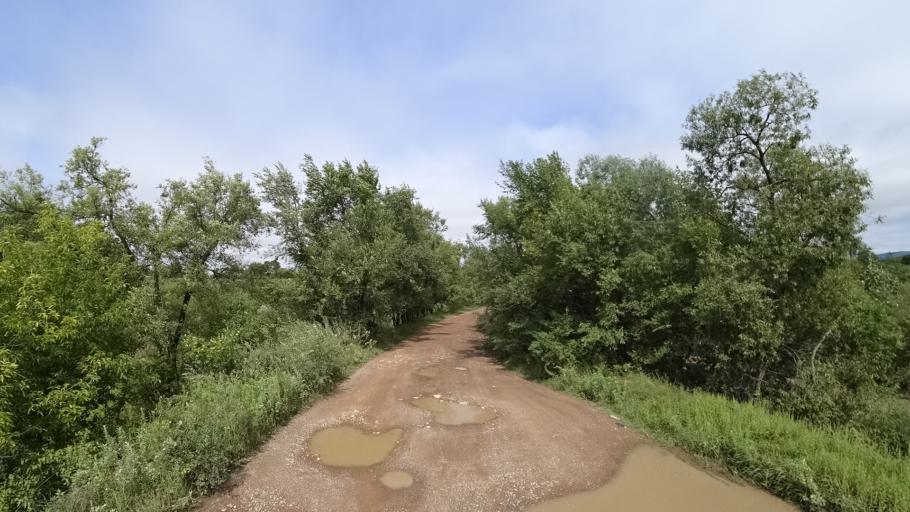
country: RU
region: Primorskiy
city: Monastyrishche
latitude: 44.1853
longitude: 132.4826
